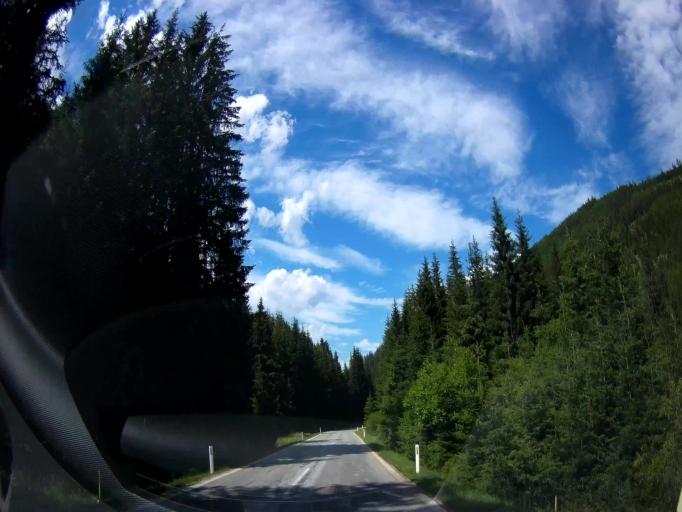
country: AT
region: Styria
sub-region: Politischer Bezirk Murau
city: Stadl an der Mur
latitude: 47.0078
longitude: 14.0095
